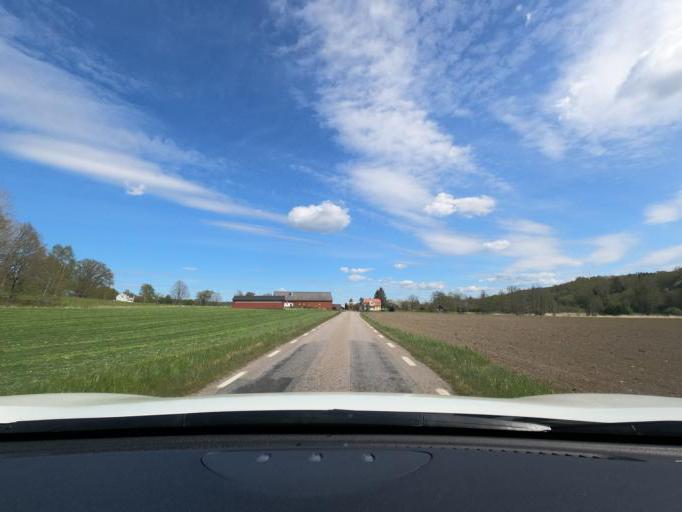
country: SE
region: Vaestra Goetaland
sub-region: Marks Kommun
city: Horred
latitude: 57.4503
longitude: 12.4715
